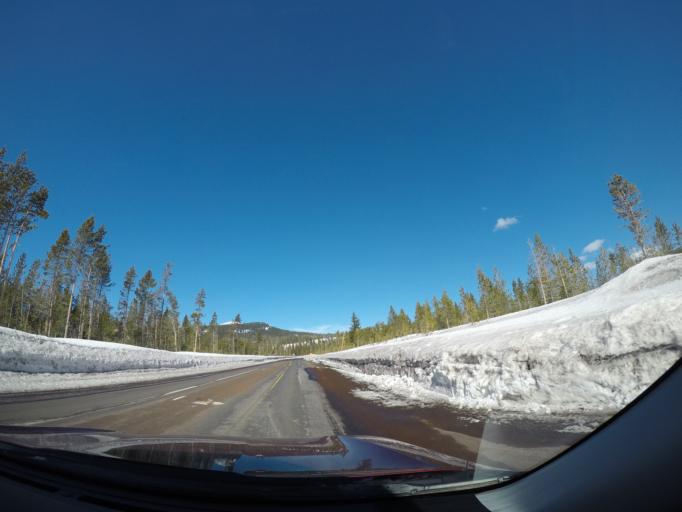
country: US
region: Oregon
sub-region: Deschutes County
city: Sunriver
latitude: 43.9791
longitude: -121.6120
